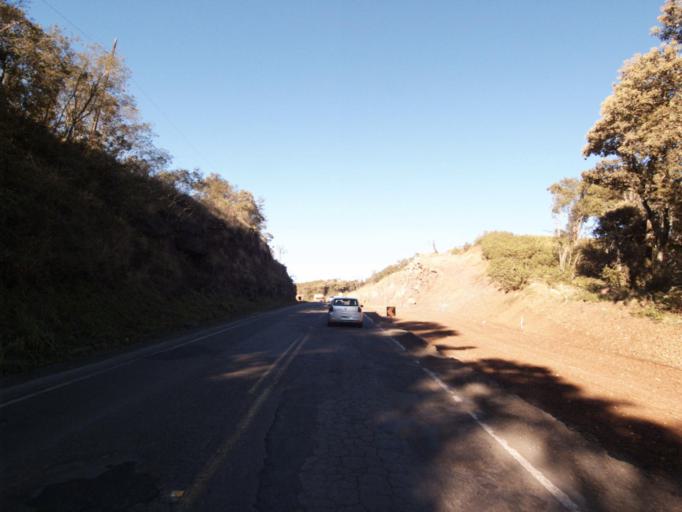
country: AR
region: Misiones
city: Bernardo de Irigoyen
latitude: -26.6323
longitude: -53.5184
